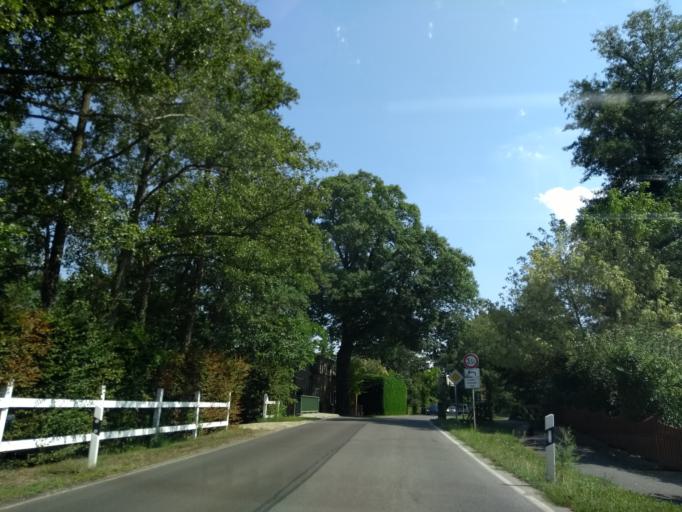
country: DE
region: Brandenburg
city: Burg
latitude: 51.8419
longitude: 14.1258
